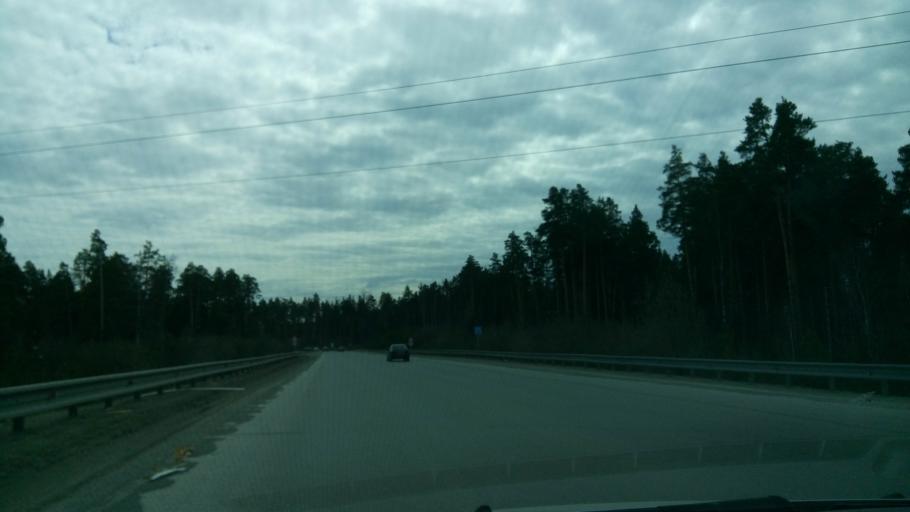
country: RU
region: Sverdlovsk
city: Verkhnyaya Pyshma
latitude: 56.9414
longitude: 60.6325
